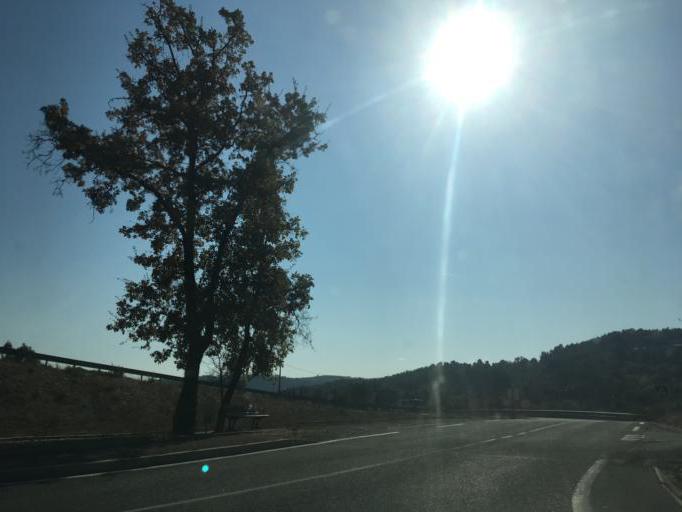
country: FR
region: Provence-Alpes-Cote d'Azur
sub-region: Departement du Var
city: Figanieres
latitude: 43.5702
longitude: 6.5066
